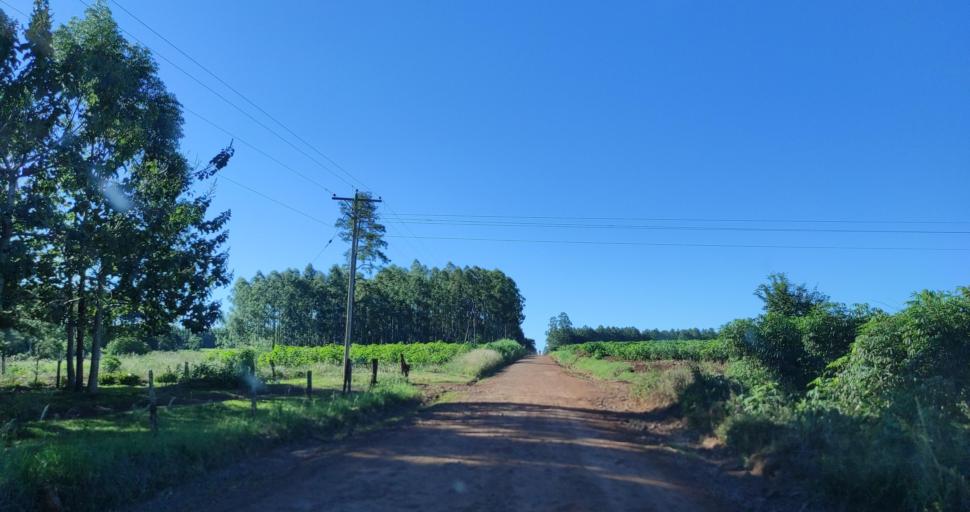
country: AR
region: Misiones
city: Capiovi
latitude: -26.8897
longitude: -54.9971
